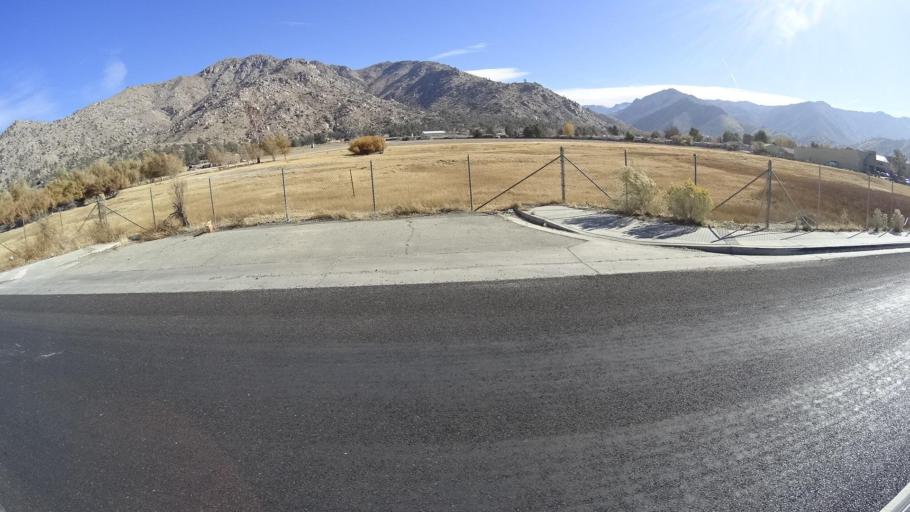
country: US
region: California
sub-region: Kern County
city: Lake Isabella
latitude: 35.6197
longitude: -118.4785
